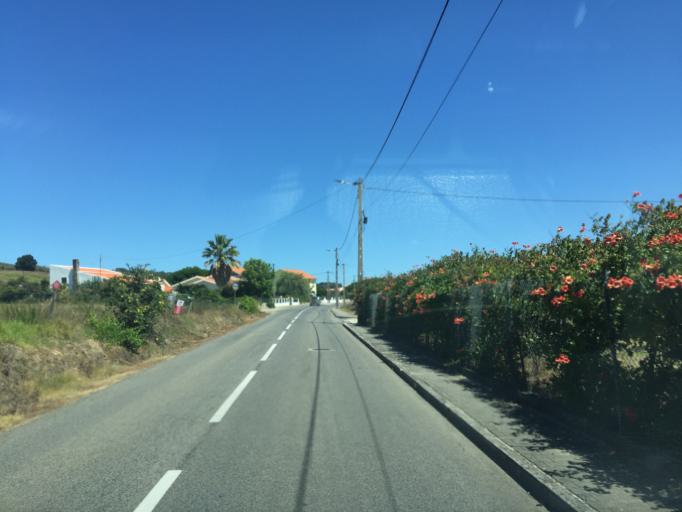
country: PT
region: Lisbon
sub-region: Torres Vedras
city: A dos Cunhados
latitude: 39.1839
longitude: -9.3111
